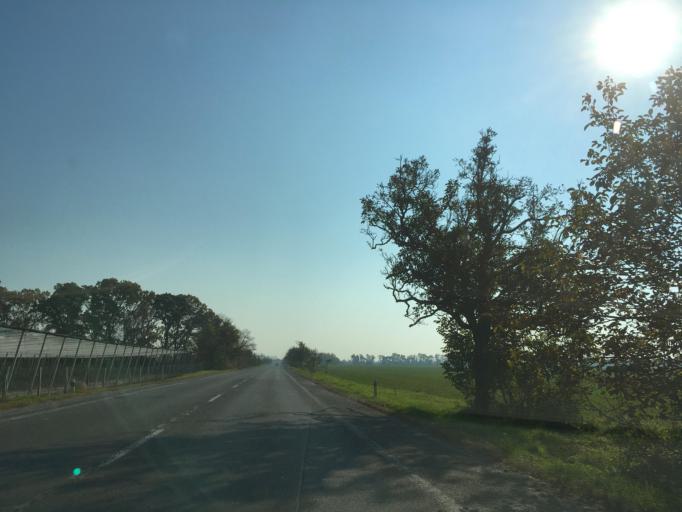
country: SK
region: Bratislavsky
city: Dunajska Luzna
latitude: 48.0703
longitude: 17.2757
